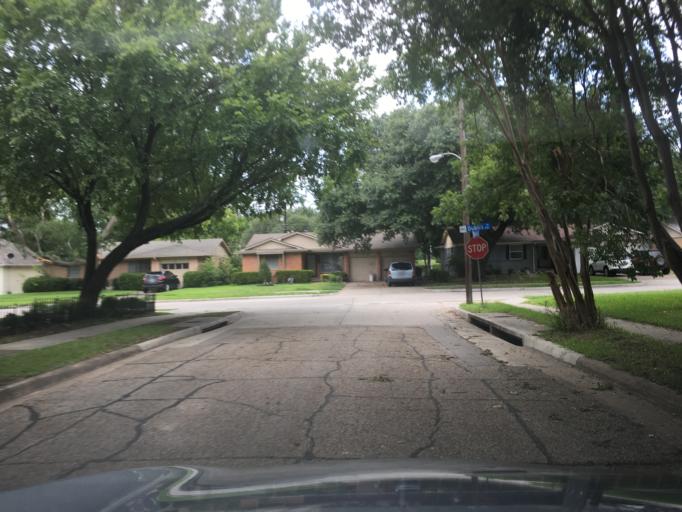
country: US
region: Texas
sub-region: Dallas County
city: Richardson
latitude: 32.9476
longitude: -96.7621
